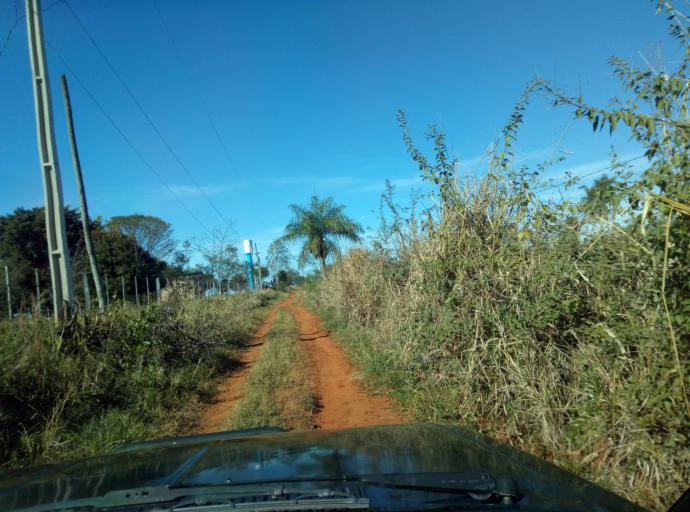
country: PY
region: Caaguazu
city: Doctor Cecilio Baez
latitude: -25.1827
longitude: -56.2423
